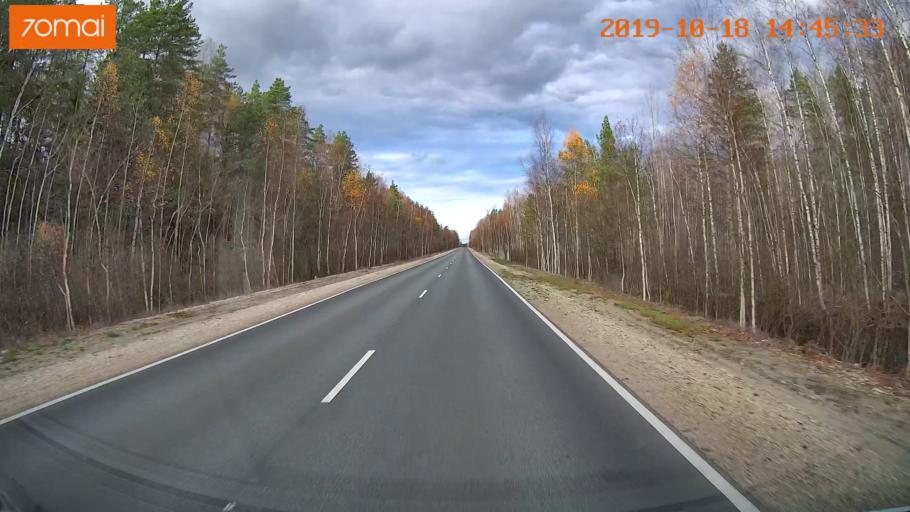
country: RU
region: Vladimir
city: Velikodvorskiy
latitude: 55.3569
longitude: 40.6792
